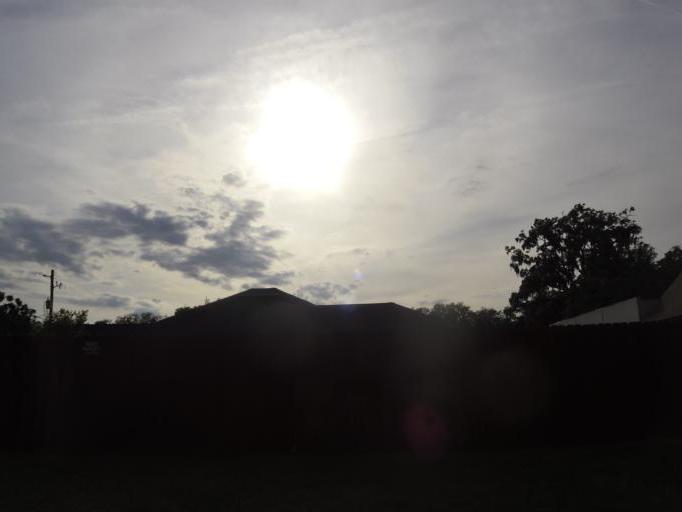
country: US
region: Florida
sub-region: Duval County
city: Jacksonville
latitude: 30.3320
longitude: -81.5994
